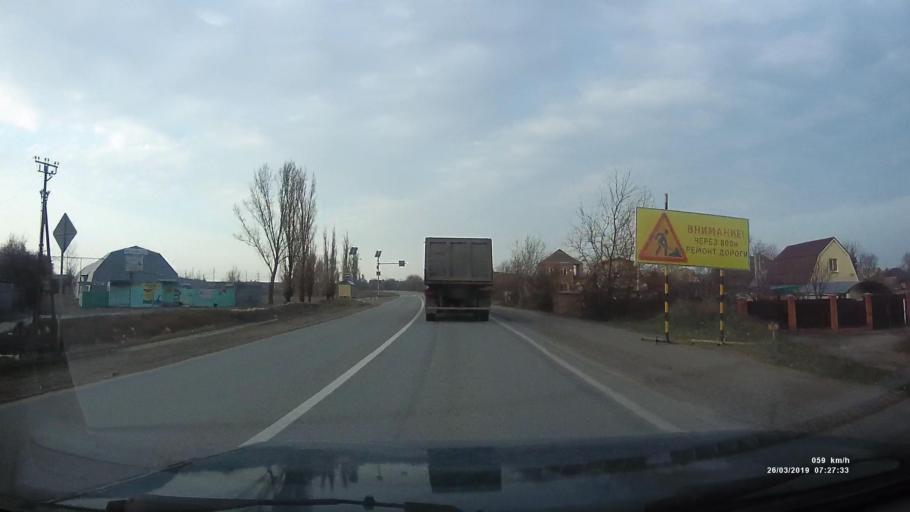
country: RU
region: Rostov
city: Taganrog
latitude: 47.2617
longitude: 38.8273
